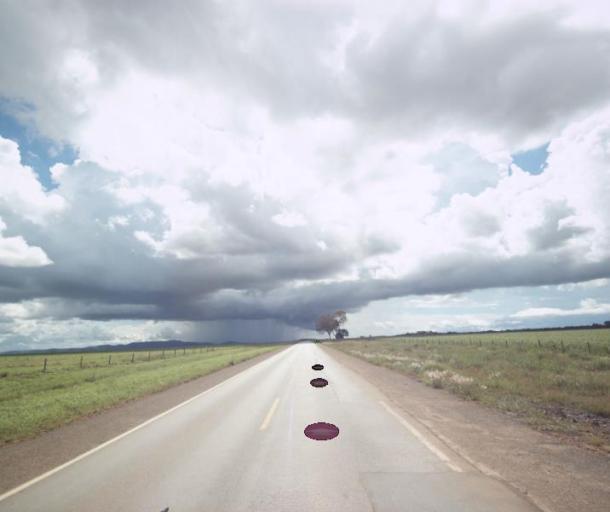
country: BR
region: Goias
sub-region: Uruacu
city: Uruacu
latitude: -14.6974
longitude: -49.1124
